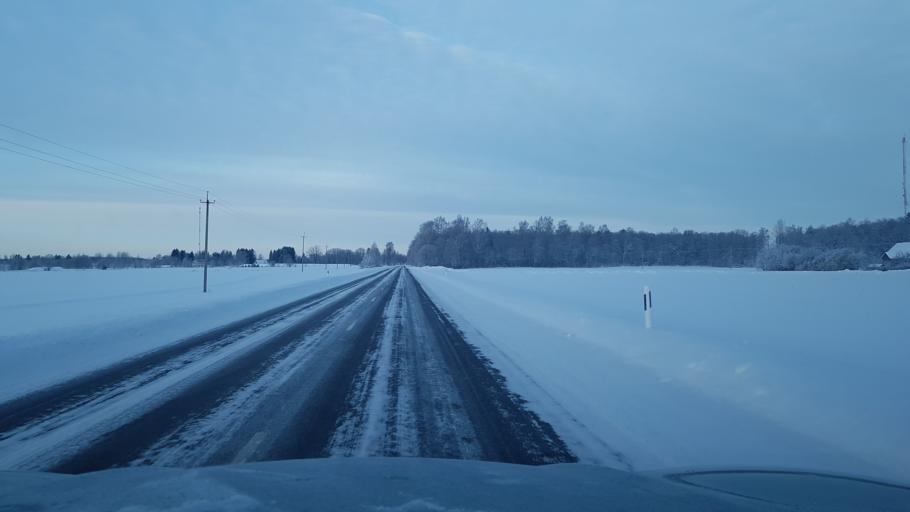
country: EE
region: Ida-Virumaa
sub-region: Johvi vald
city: Johvi
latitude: 59.3435
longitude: 27.4496
